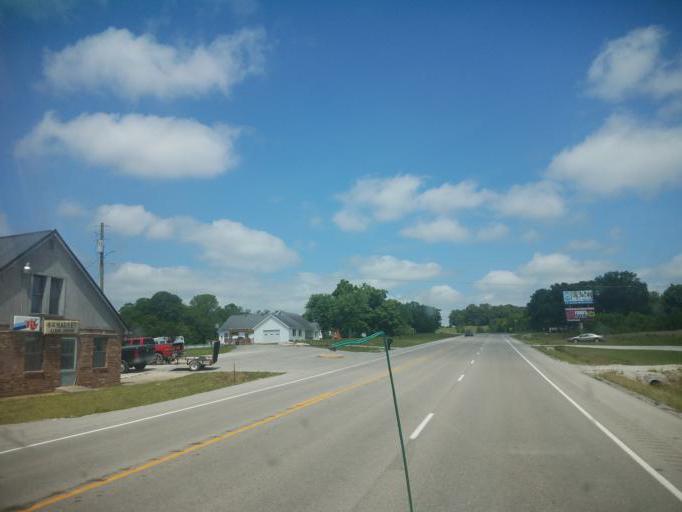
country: US
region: Kentucky
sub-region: Barren County
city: Glasgow
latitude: 36.9453
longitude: -85.8379
